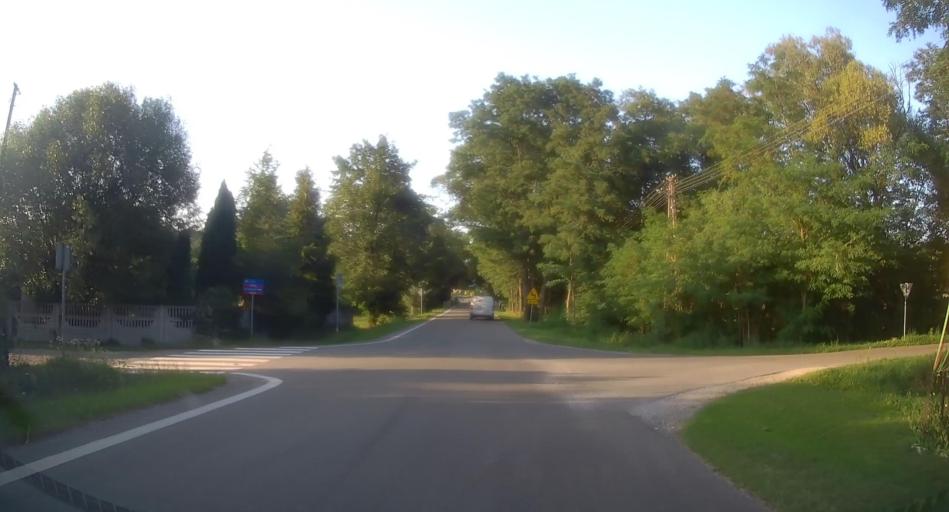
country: PL
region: Masovian Voivodeship
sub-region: Powiat zyrardowski
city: Puszcza Marianska
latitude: 51.9079
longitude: 20.3429
